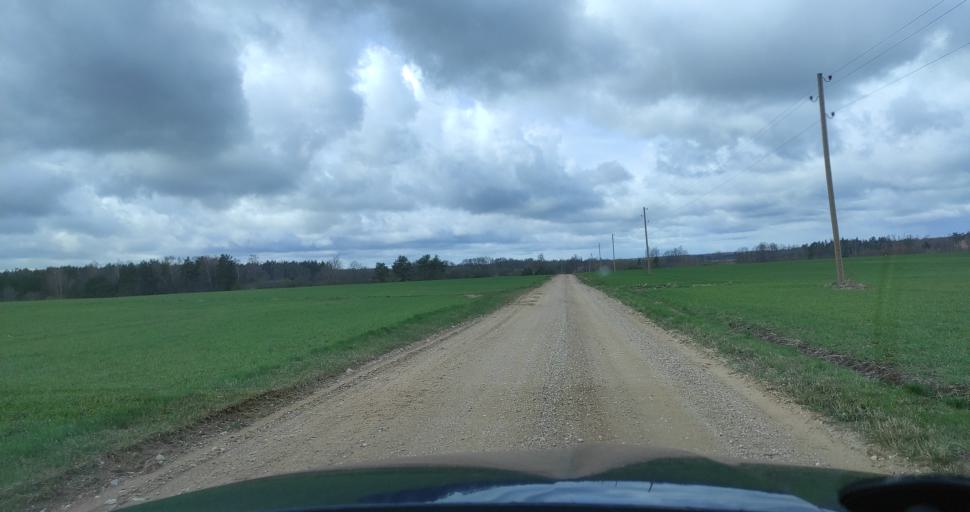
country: LV
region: Kuldigas Rajons
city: Kuldiga
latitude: 57.0567
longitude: 21.7787
